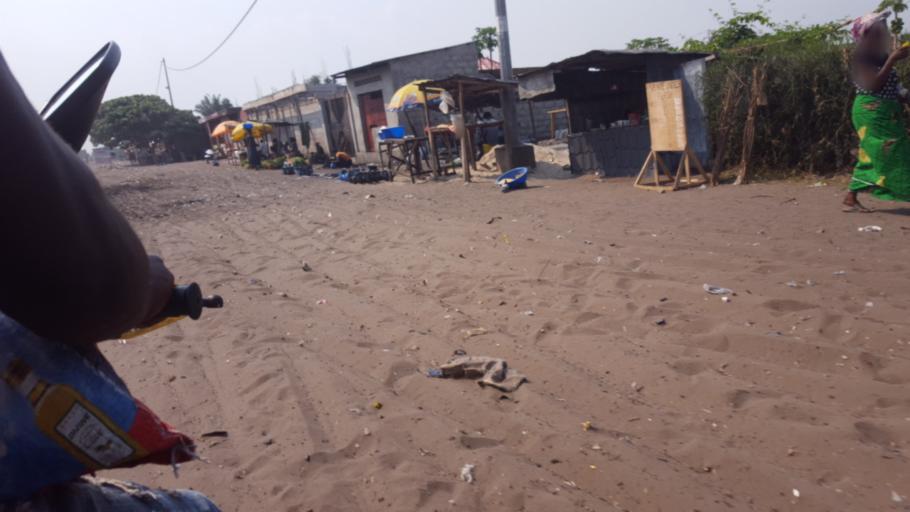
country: CD
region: Kinshasa
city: Masina
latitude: -4.3641
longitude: 15.5110
